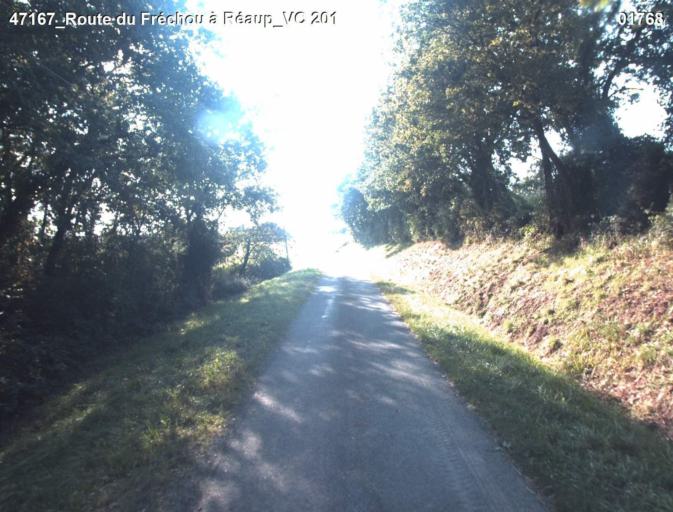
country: FR
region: Aquitaine
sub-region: Departement du Lot-et-Garonne
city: Mezin
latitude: 44.0739
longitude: 0.2938
